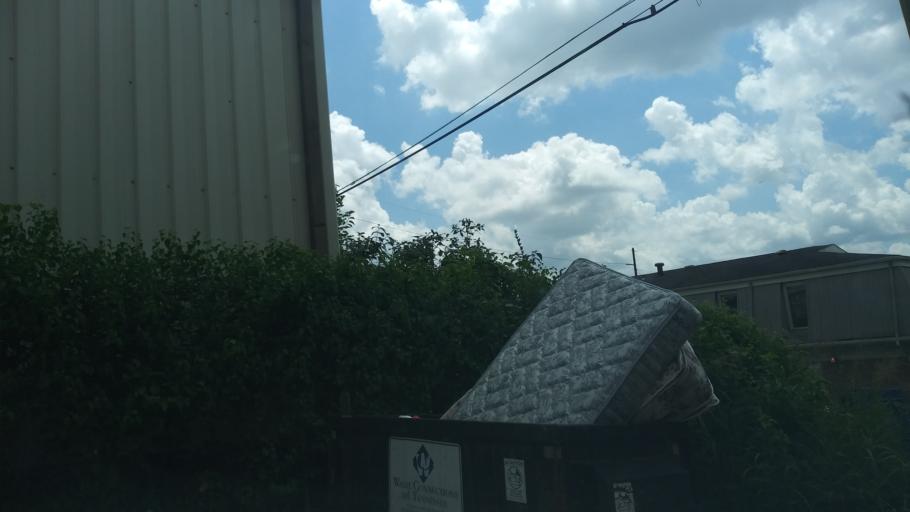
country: US
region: Tennessee
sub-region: Davidson County
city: Nashville
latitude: 36.1274
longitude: -86.7755
